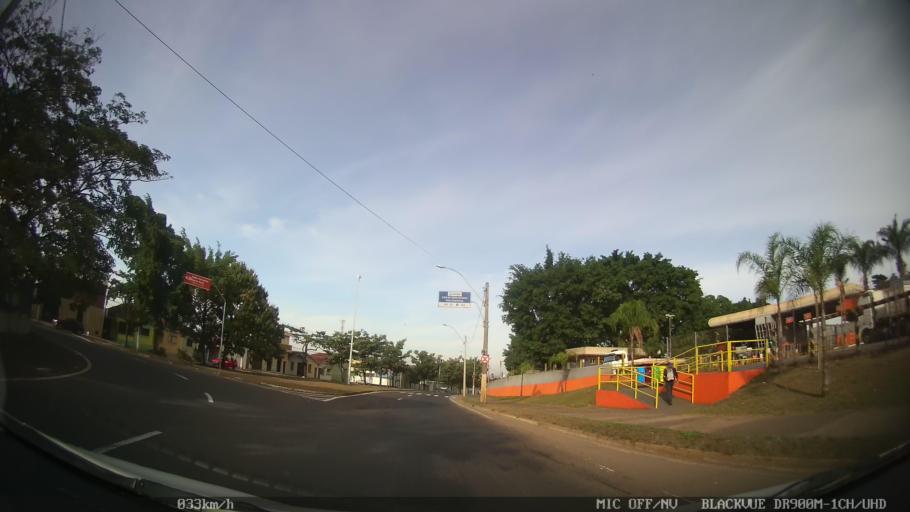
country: BR
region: Sao Paulo
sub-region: Piracicaba
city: Piracicaba
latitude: -22.6989
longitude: -47.6547
